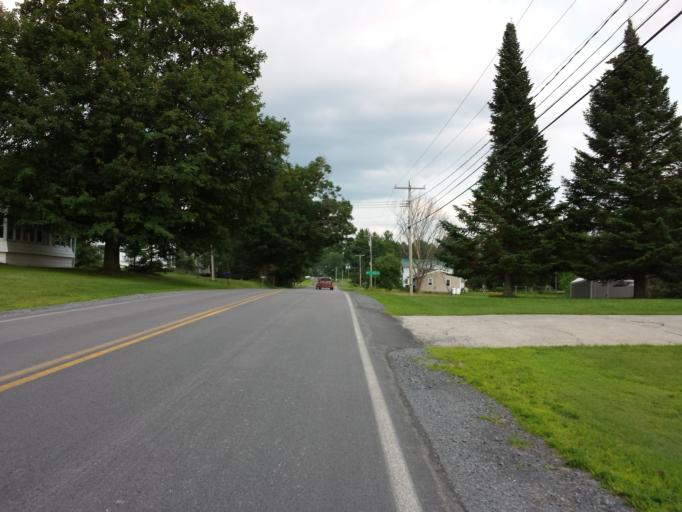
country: US
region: New York
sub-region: St. Lawrence County
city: Potsdam
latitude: 44.7179
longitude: -74.9077
